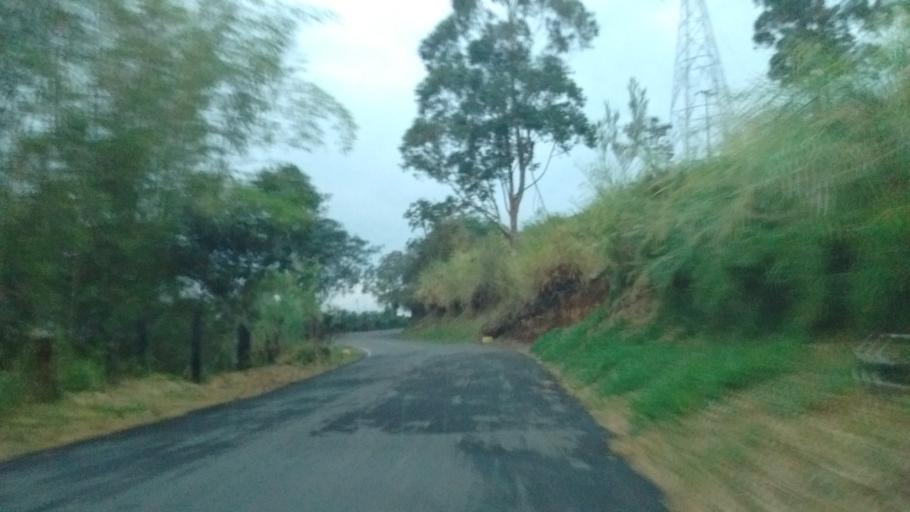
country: CO
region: Cauca
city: Popayan
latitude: 2.3746
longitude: -76.6981
